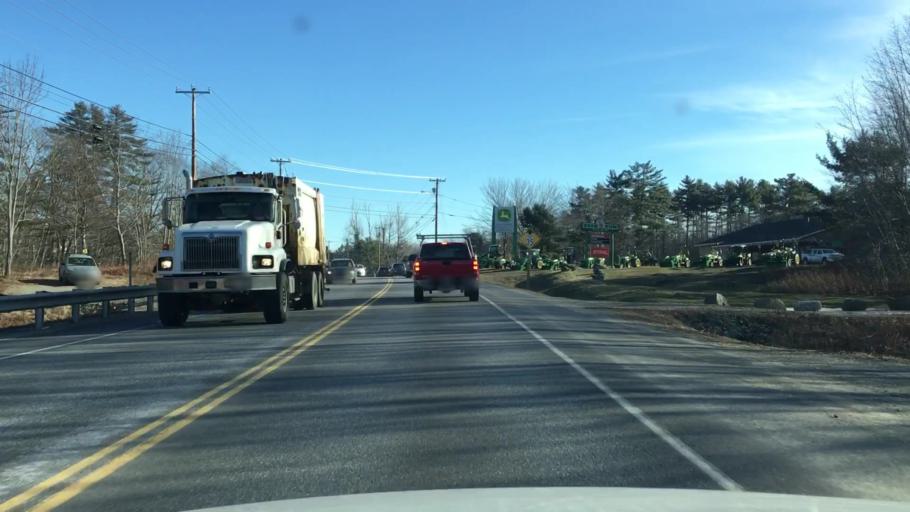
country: US
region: Maine
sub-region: Hancock County
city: Ellsworth
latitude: 44.5644
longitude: -68.4440
